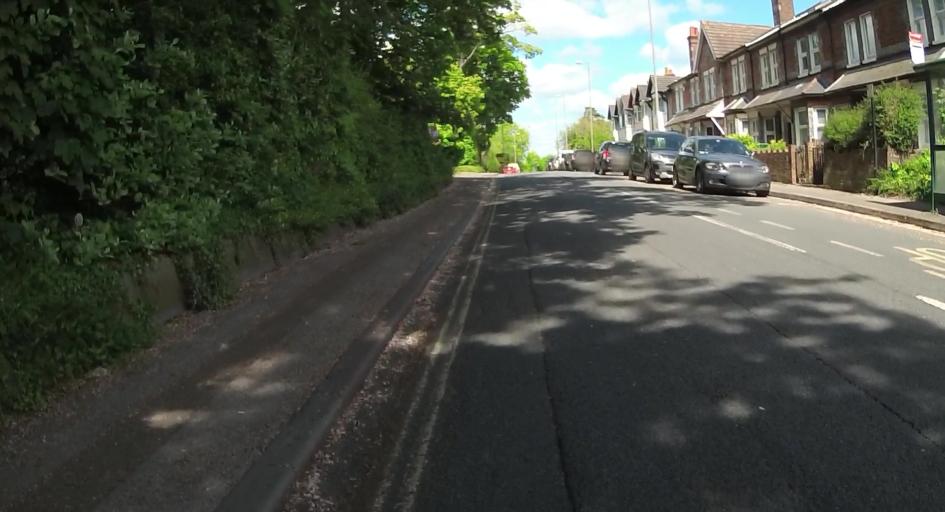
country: GB
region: England
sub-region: Hampshire
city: Basingstoke
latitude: 51.2712
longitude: -1.0790
